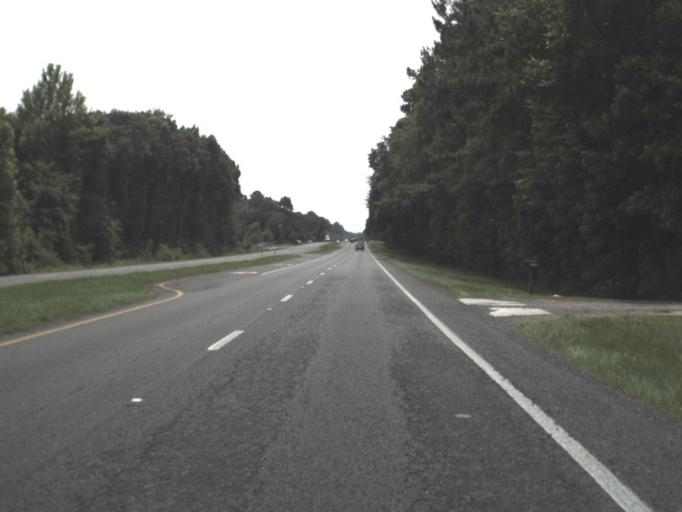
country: US
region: Florida
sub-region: Nassau County
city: Nassau Village-Ratliff
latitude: 30.5355
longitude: -81.8096
